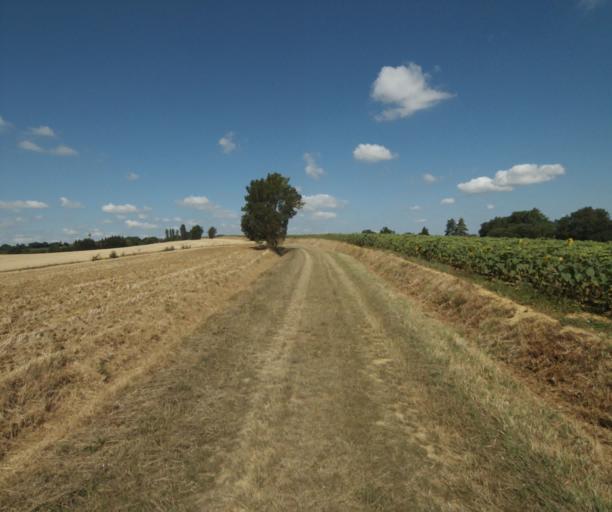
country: FR
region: Midi-Pyrenees
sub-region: Departement de la Haute-Garonne
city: Auriac-sur-Vendinelle
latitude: 43.4675
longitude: 1.7907
